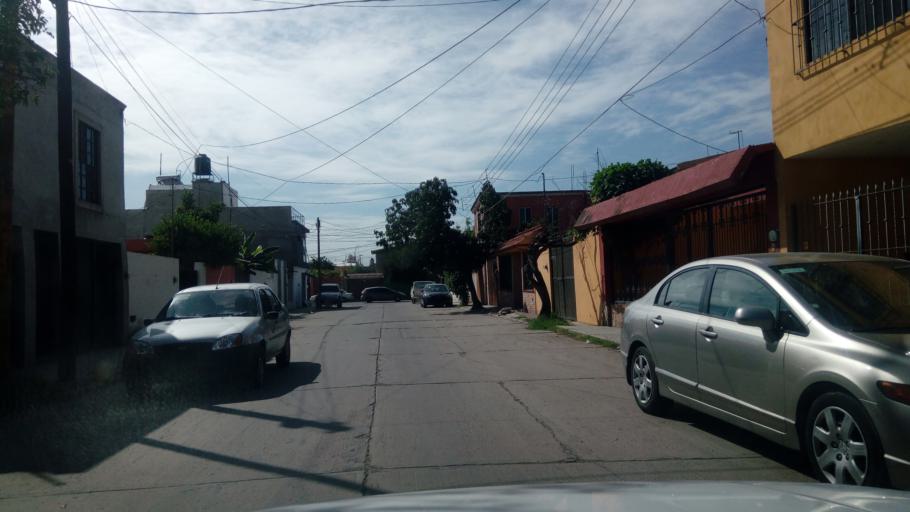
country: MX
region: Durango
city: Victoria de Durango
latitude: 24.0043
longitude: -104.6674
